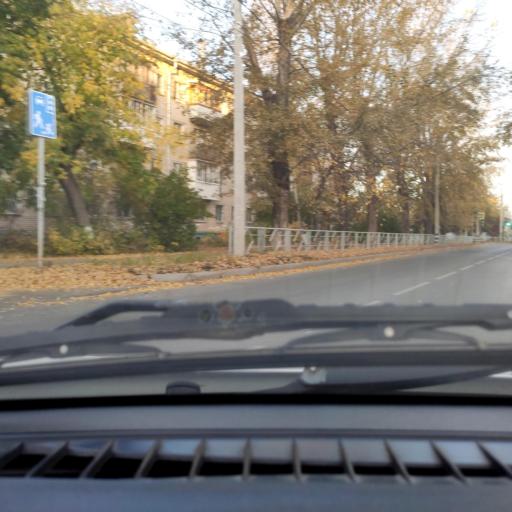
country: RU
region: Samara
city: Tol'yatti
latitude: 53.5104
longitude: 49.4050
